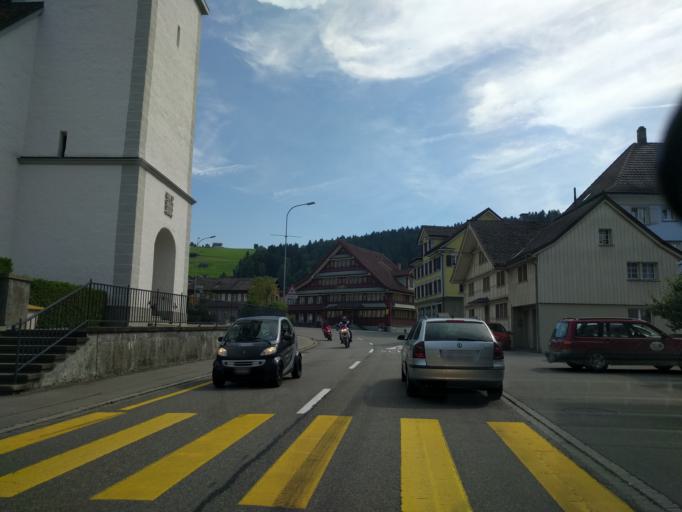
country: CH
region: Saint Gallen
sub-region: Wahlkreis Toggenburg
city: Sankt Peterzell
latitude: 47.3184
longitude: 9.1736
